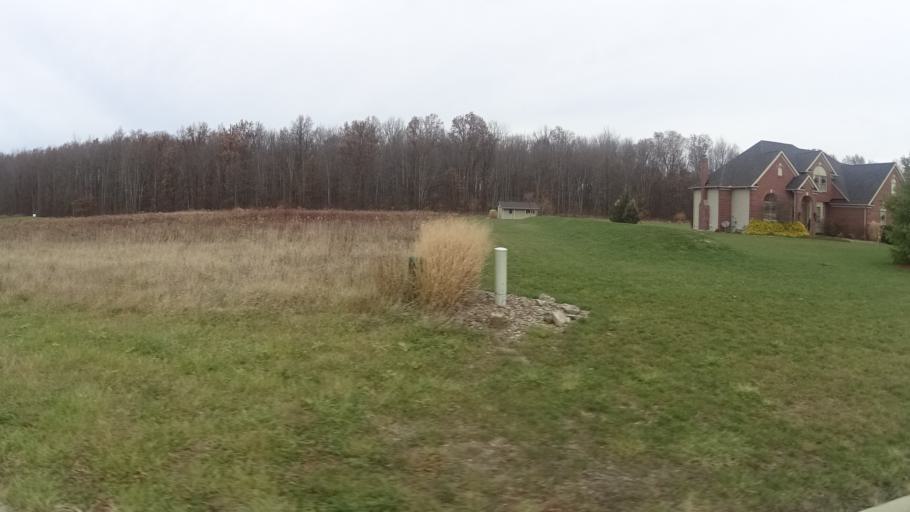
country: US
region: Ohio
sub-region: Cuyahoga County
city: Olmsted Falls
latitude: 41.3461
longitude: -81.9482
